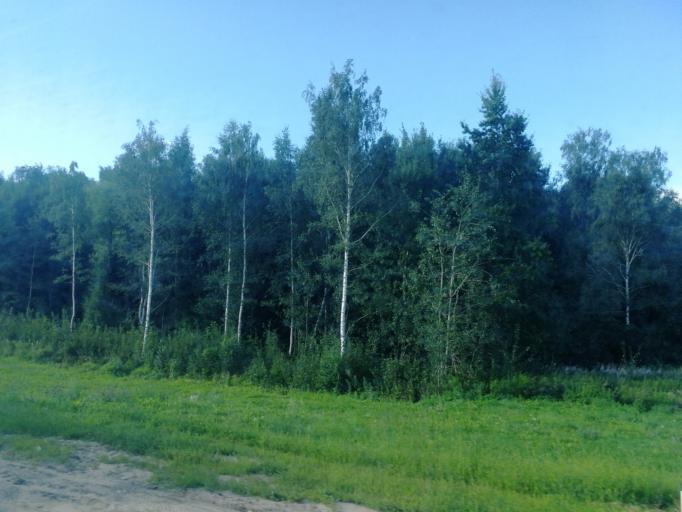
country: RU
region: Tula
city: Leninskiy
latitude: 54.2339
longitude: 37.3571
